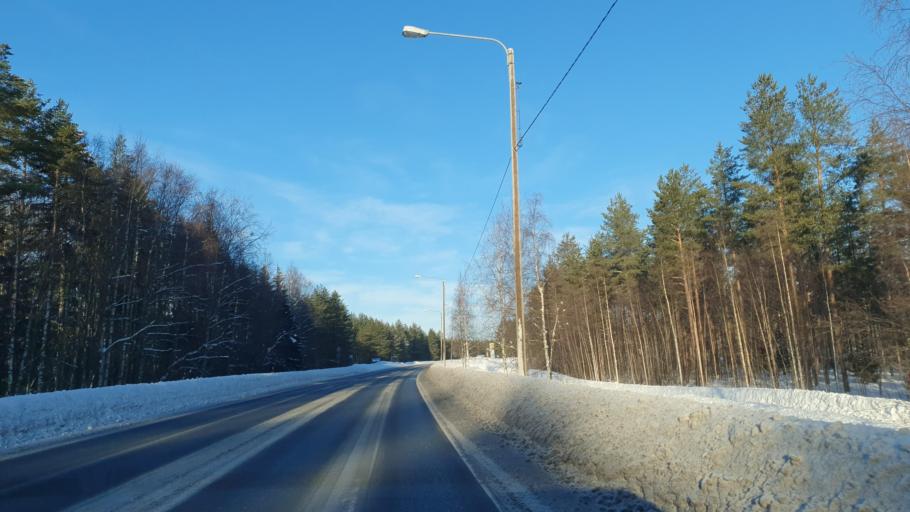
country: FI
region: Northern Ostrobothnia
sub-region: Oulu
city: Tyrnaevae
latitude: 64.9121
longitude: 25.7676
